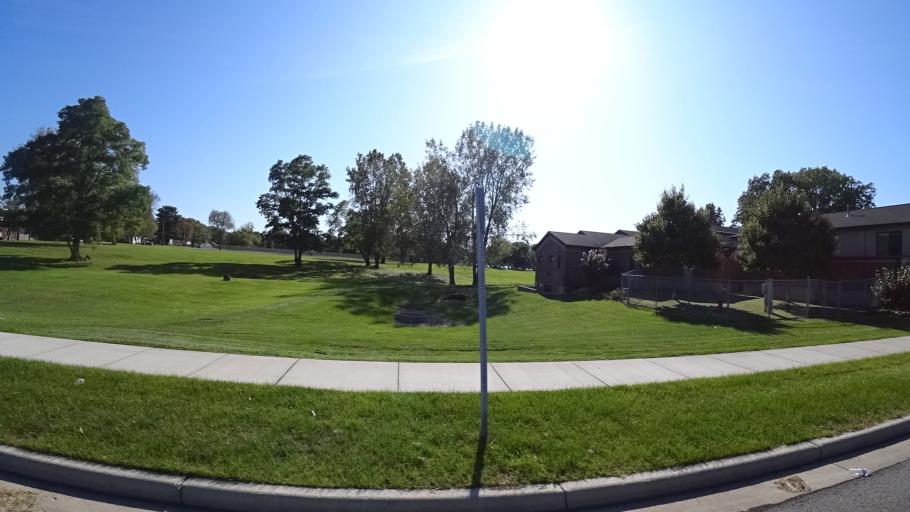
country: US
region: Indiana
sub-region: LaPorte County
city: Trail Creek
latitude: 41.7081
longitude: -86.8676
